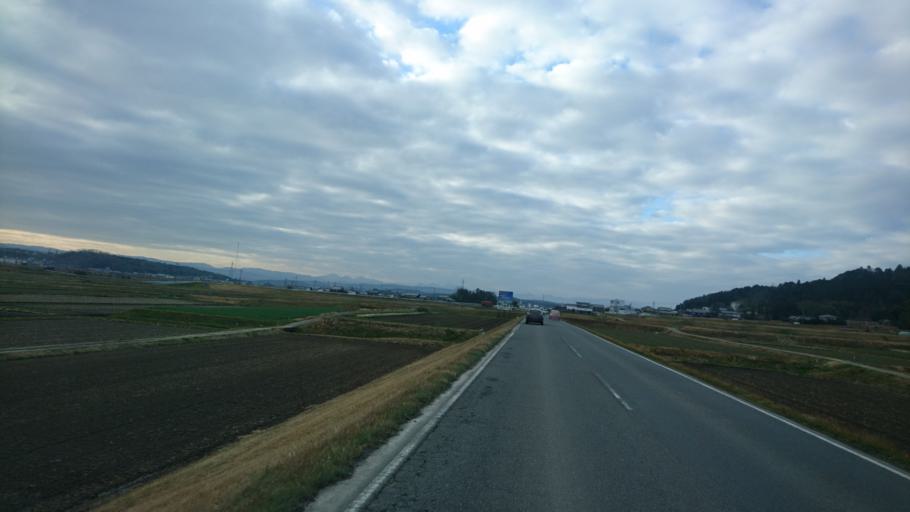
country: JP
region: Mie
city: Ueno-ebisumachi
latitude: 34.7626
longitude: 136.1093
